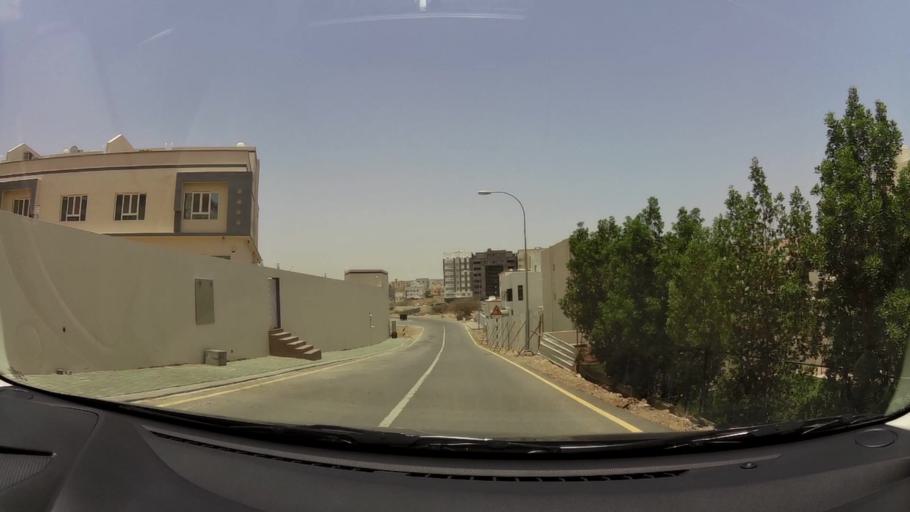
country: OM
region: Muhafazat Masqat
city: Bawshar
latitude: 23.5618
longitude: 58.4220
